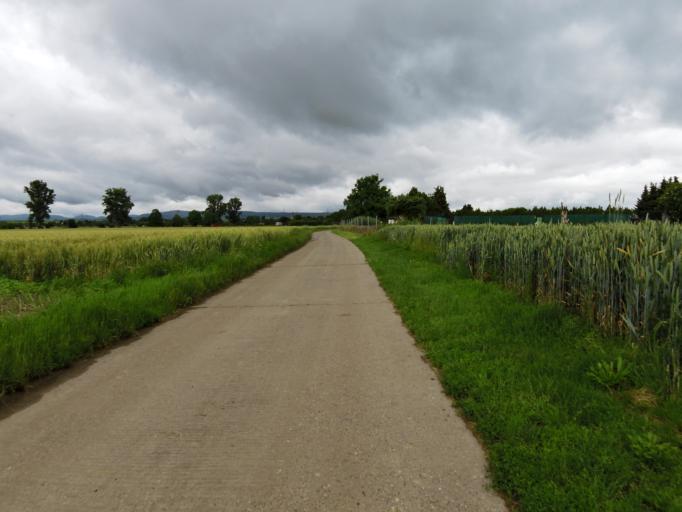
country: DE
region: Rheinland-Pfalz
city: Dirmstein
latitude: 49.5600
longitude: 8.2530
